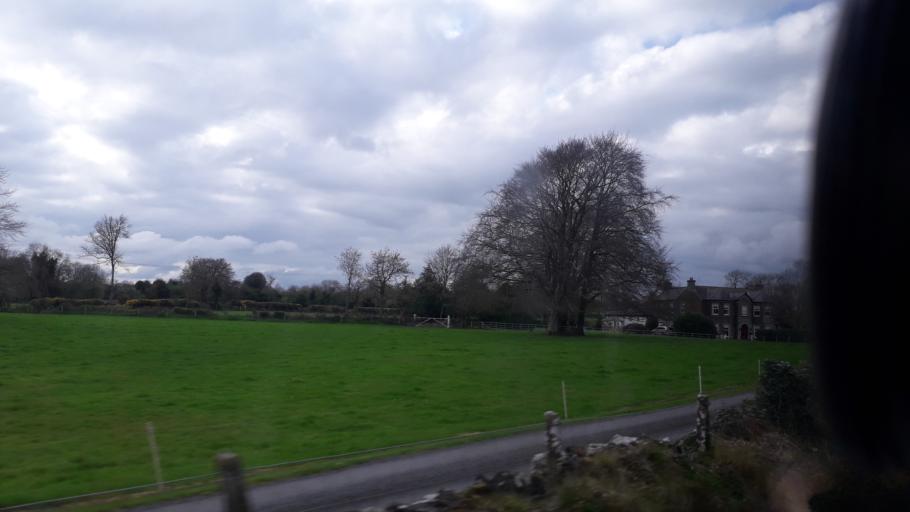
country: IE
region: Leinster
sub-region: An Iarmhi
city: An Muileann gCearr
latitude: 53.6171
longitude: -7.4117
